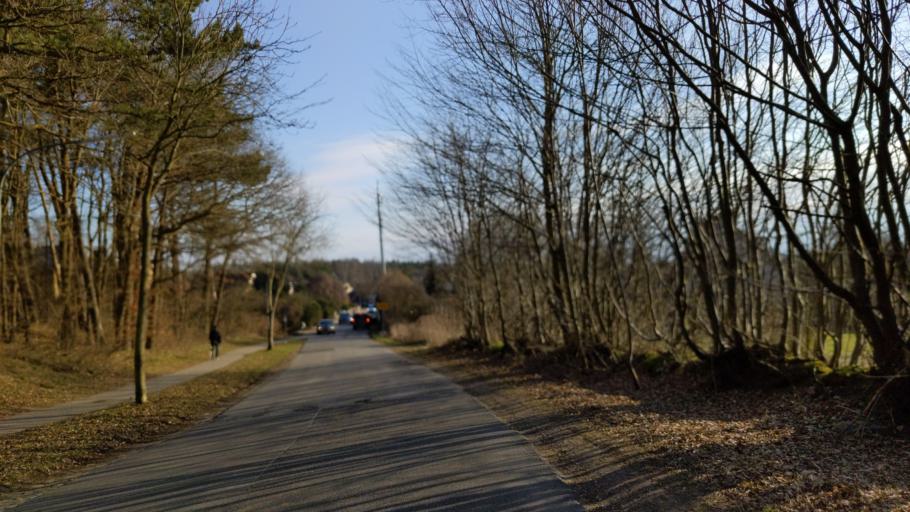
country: DE
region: Schleswig-Holstein
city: Ratekau
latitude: 53.9741
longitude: 10.7010
